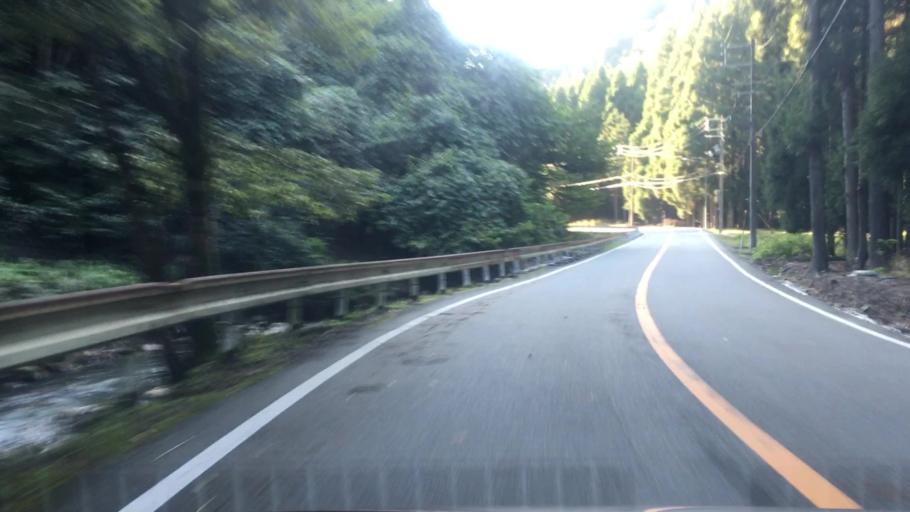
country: JP
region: Hyogo
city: Toyooka
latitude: 35.6165
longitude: 134.8573
